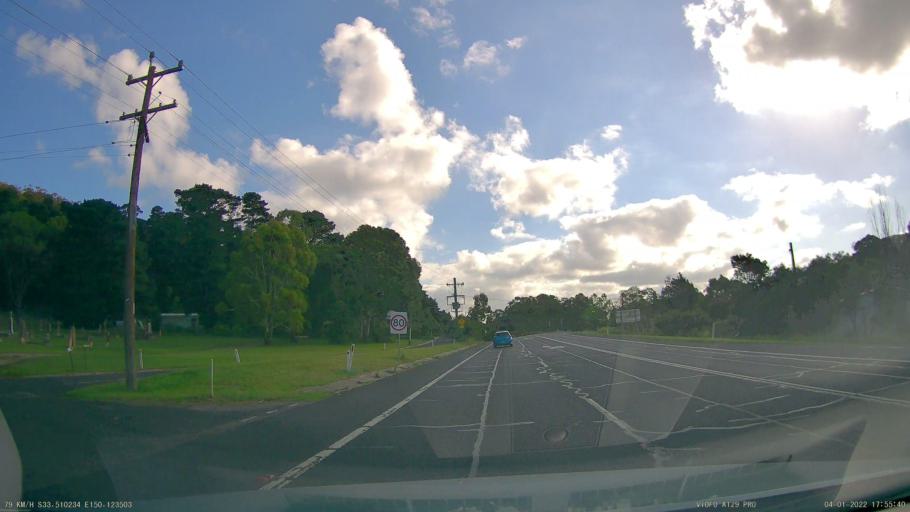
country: AU
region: New South Wales
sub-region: Lithgow
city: Bowenfels
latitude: -33.5103
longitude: 150.1237
